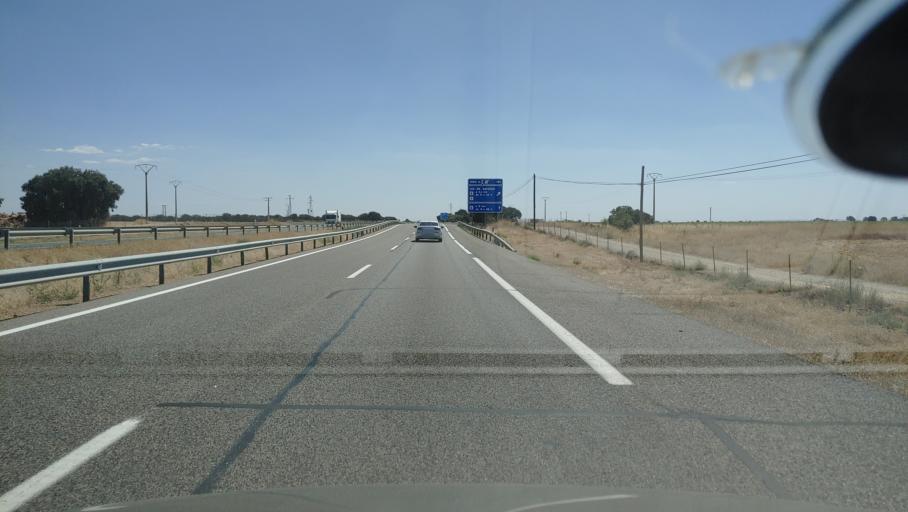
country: ES
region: Castille-La Mancha
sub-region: Provincia de Ciudad Real
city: Villarta de San Juan
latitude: 39.1951
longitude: -3.4041
